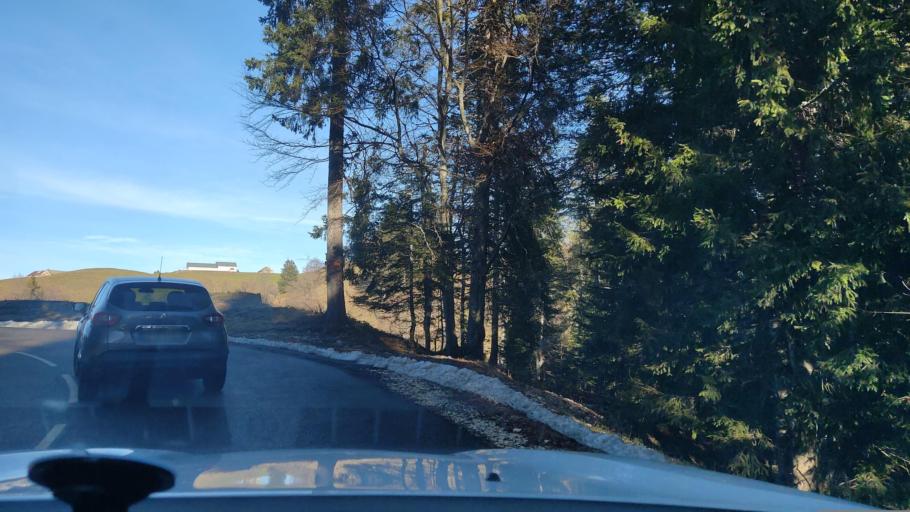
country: FR
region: Rhone-Alpes
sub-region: Departement de la Savoie
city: Mouxy
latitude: 45.6677
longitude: 5.9778
